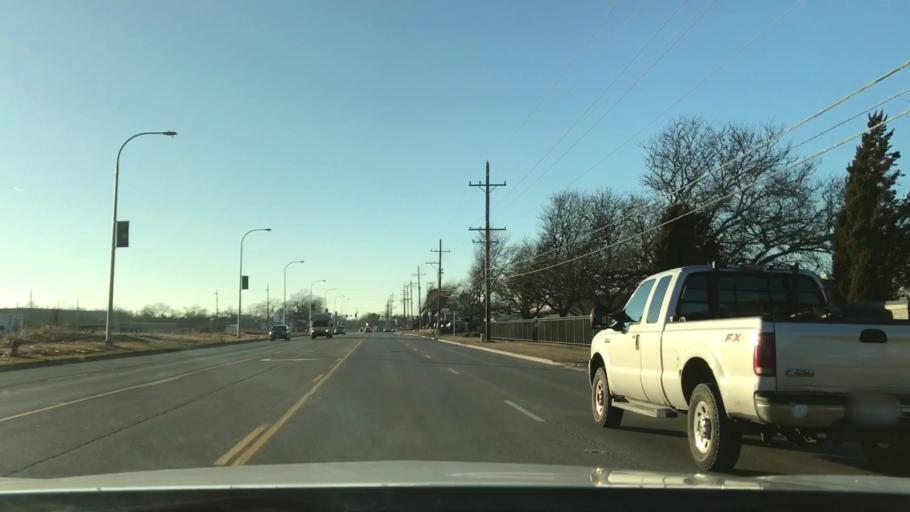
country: US
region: Illinois
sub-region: Kane County
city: Elgin
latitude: 42.0585
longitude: -88.3109
